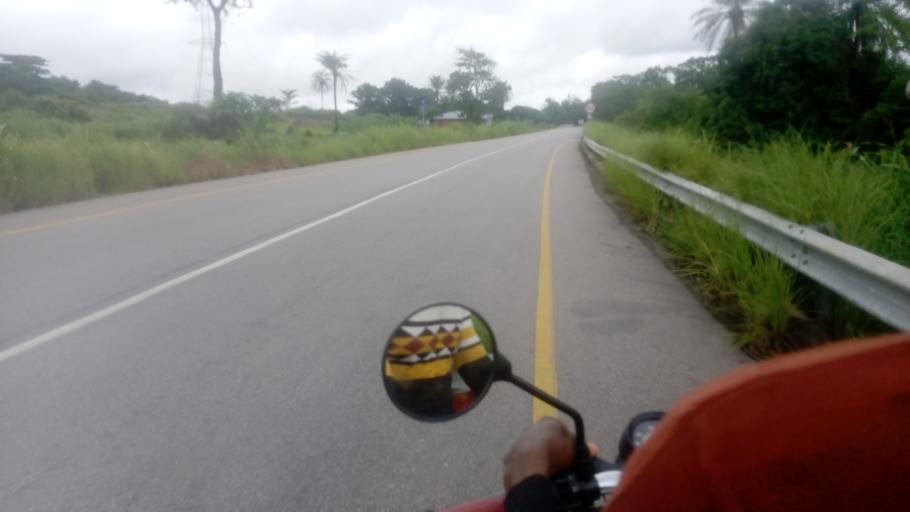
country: SL
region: Northern Province
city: Masaka
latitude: 8.6474
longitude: -11.7616
